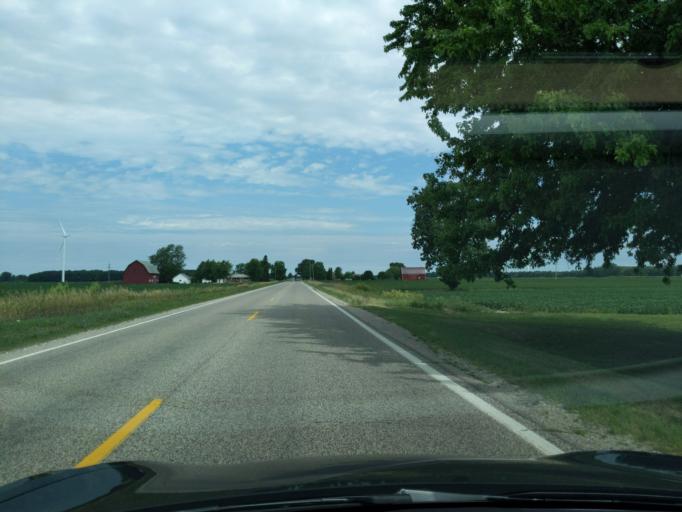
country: US
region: Michigan
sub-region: Gratiot County
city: Breckenridge
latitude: 43.3891
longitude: -84.4293
